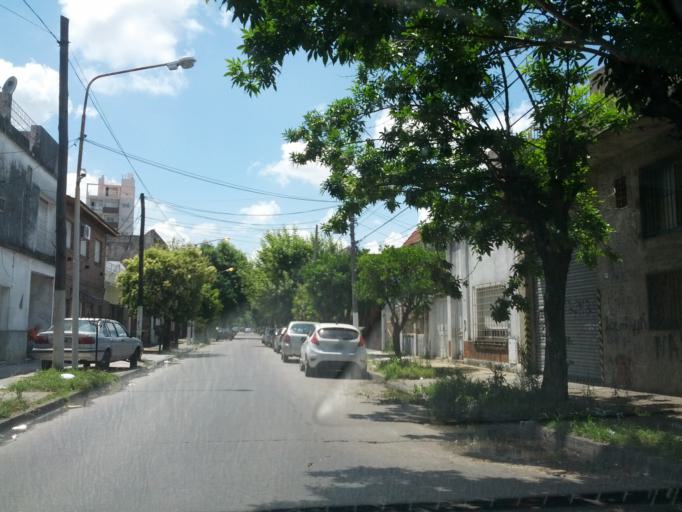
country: AR
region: Buenos Aires
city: San Justo
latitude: -34.6436
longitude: -58.5435
